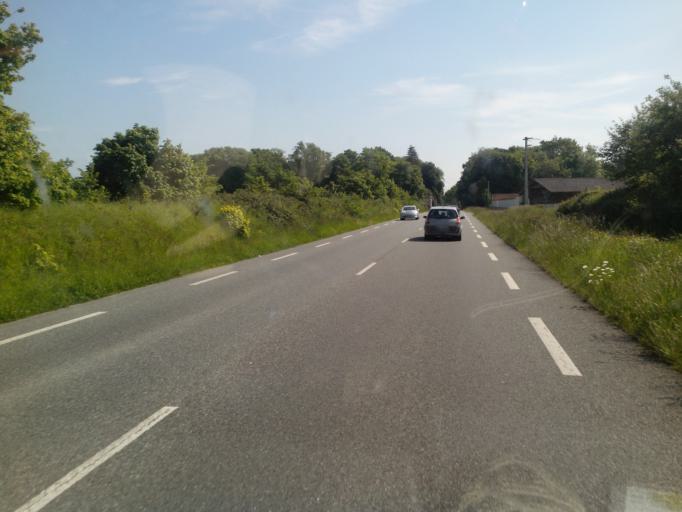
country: FR
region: Picardie
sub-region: Departement de la Somme
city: Quend
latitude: 50.3536
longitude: 1.6491
